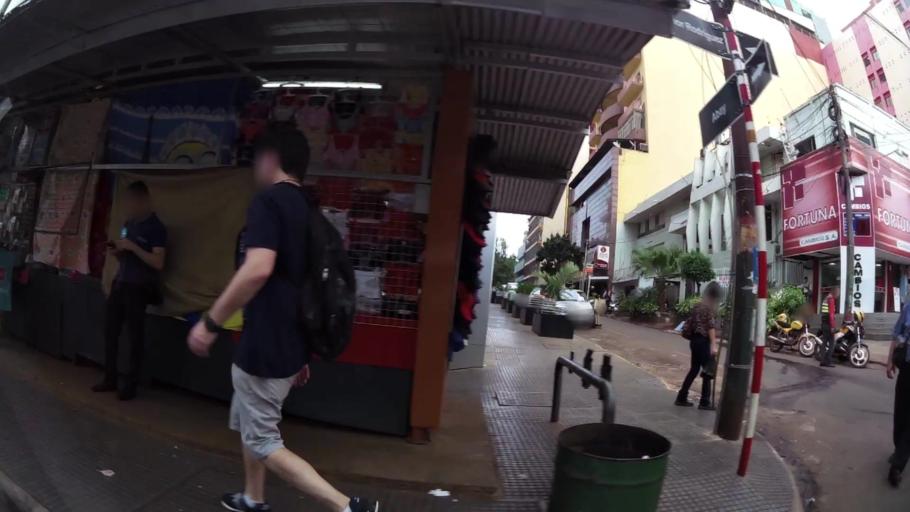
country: PY
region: Alto Parana
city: Ciudad del Este
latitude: -25.5097
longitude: -54.6111
